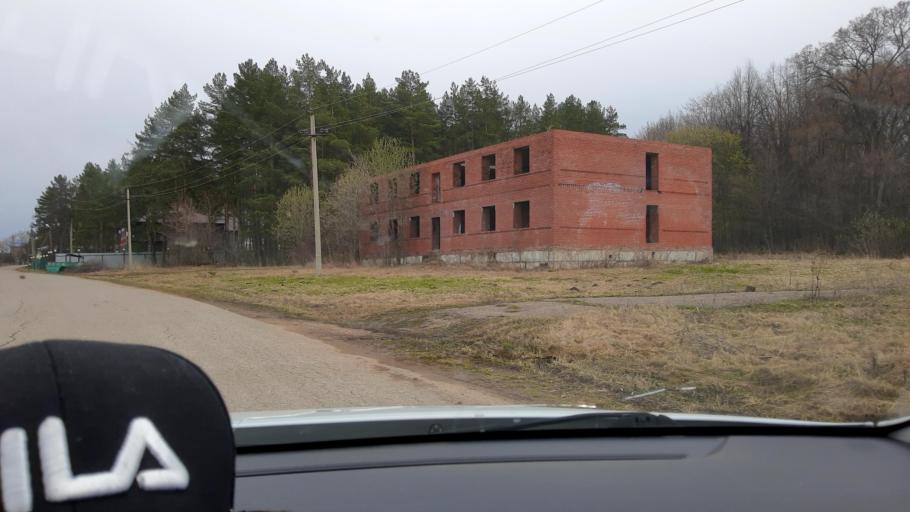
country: RU
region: Bashkortostan
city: Iglino
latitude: 54.7699
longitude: 56.5293
